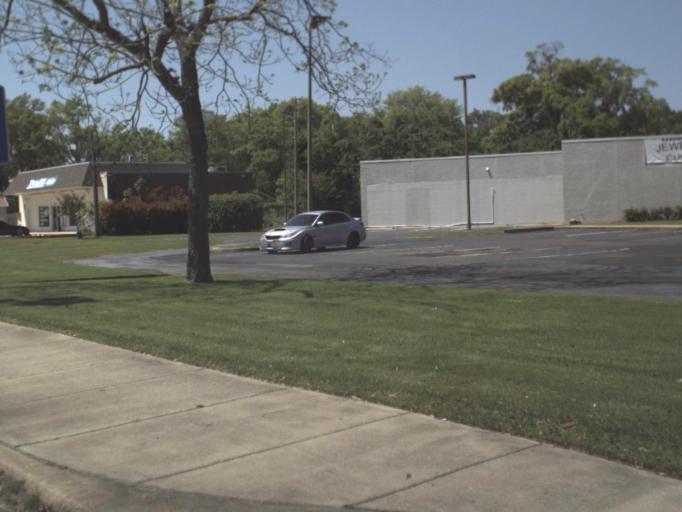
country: US
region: Florida
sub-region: Escambia County
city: Pensacola
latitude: 30.4209
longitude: -87.2447
